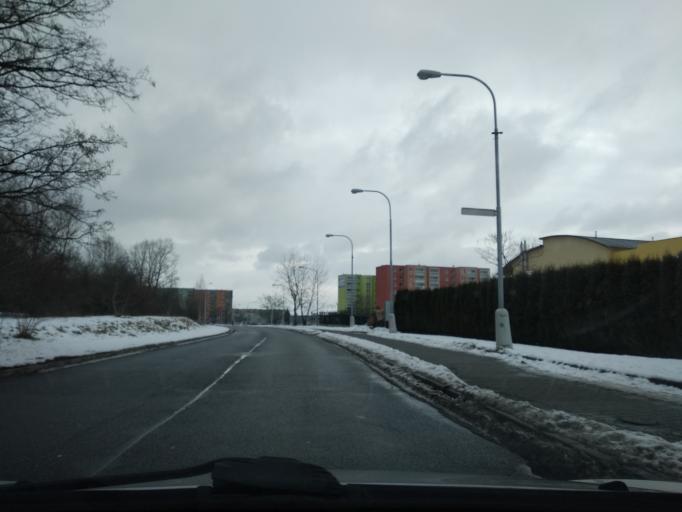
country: CZ
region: South Moravian
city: Ostopovice
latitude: 49.1723
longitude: 16.5653
